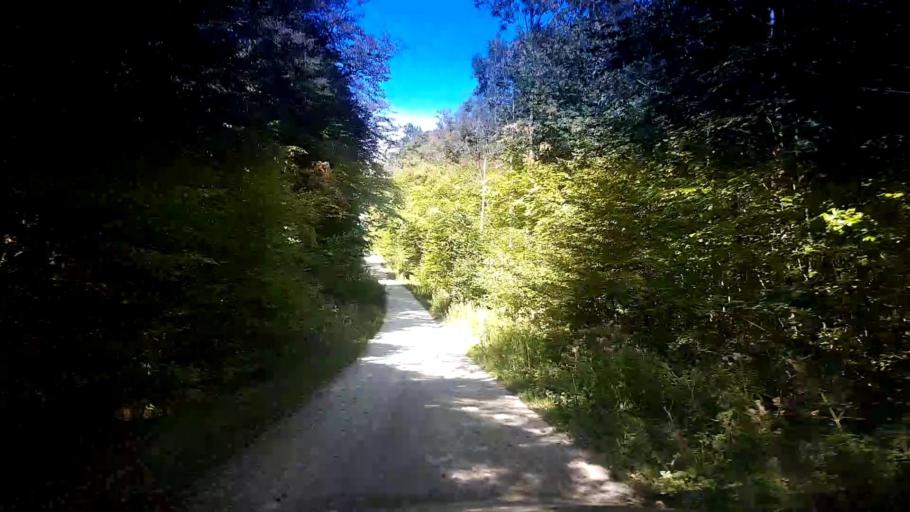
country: DE
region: Bavaria
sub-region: Upper Franconia
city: Litzendorf
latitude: 49.8888
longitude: 11.0180
